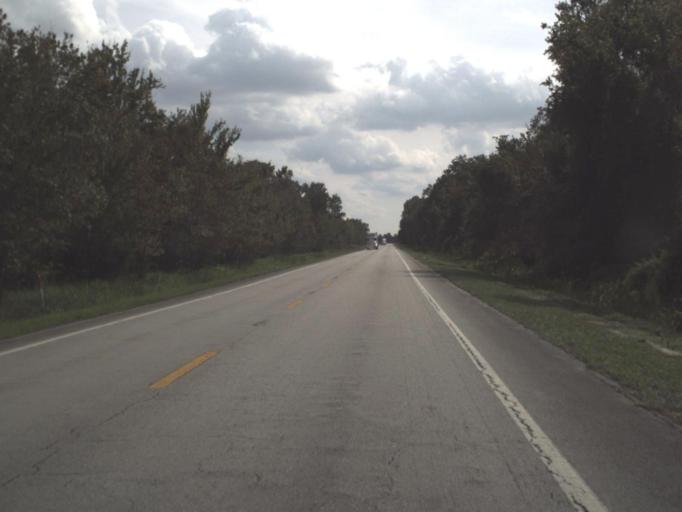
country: US
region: Florida
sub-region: Okeechobee County
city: Cypress Quarters
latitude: 27.5101
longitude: -80.8070
